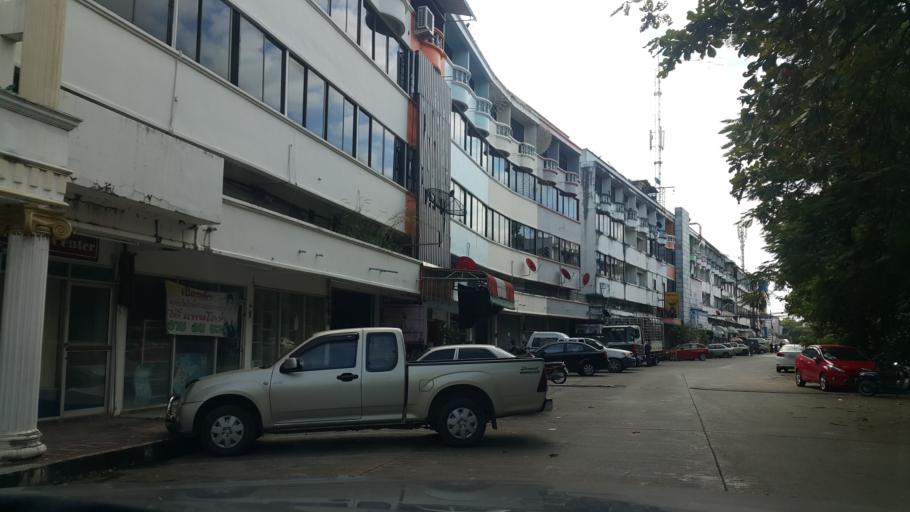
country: TH
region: Chiang Mai
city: Chiang Mai
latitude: 18.7882
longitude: 99.0148
